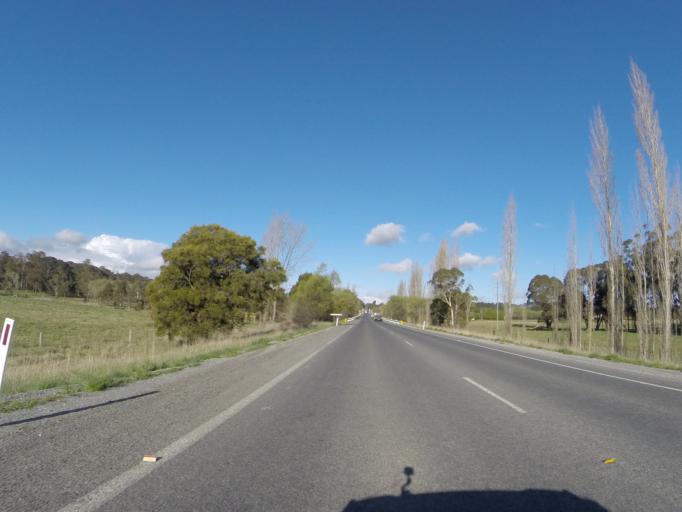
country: AU
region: New South Wales
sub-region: Wingecarribee
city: Moss Vale
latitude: -34.5732
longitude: 150.4661
